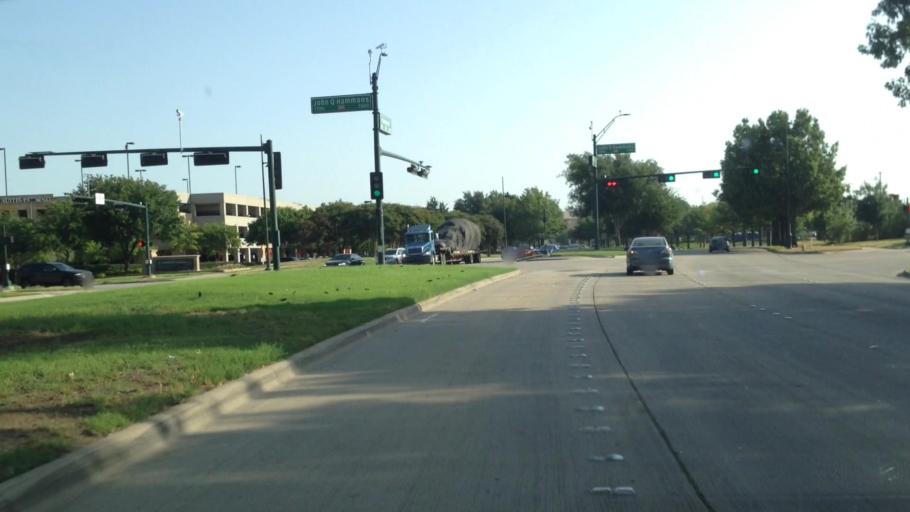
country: US
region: Texas
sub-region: Collin County
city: Frisco
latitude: 33.0985
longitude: -96.8169
